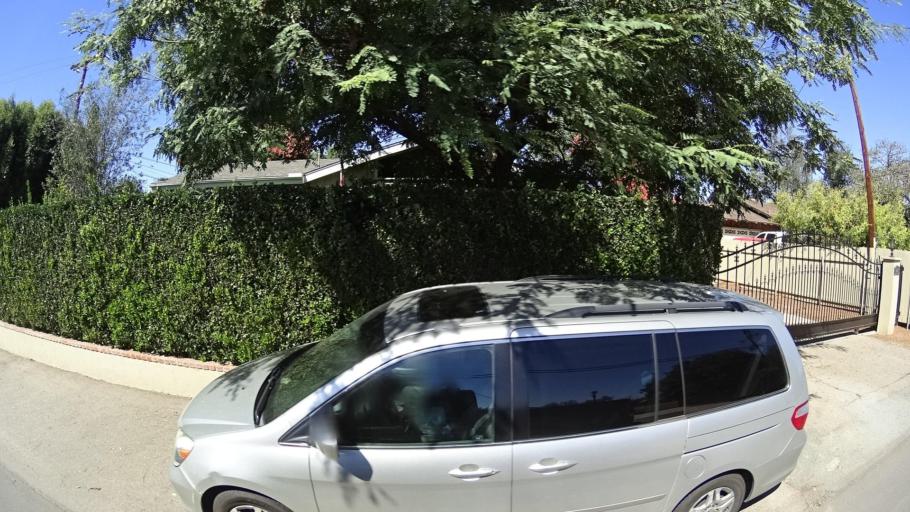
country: US
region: California
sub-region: San Diego County
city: Bonita
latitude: 32.6555
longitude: -117.0567
